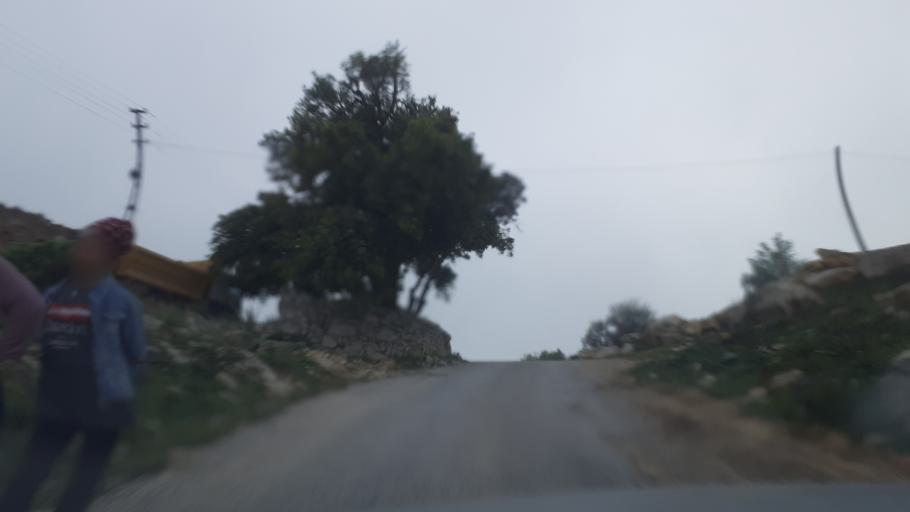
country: TR
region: Hatay
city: Yeditepe
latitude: 35.9689
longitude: 36.0063
